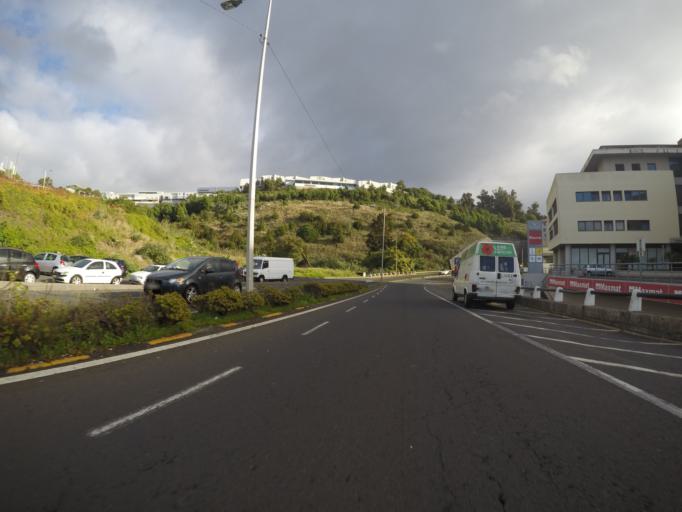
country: PT
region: Madeira
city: Canico
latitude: 32.6480
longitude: -16.8600
